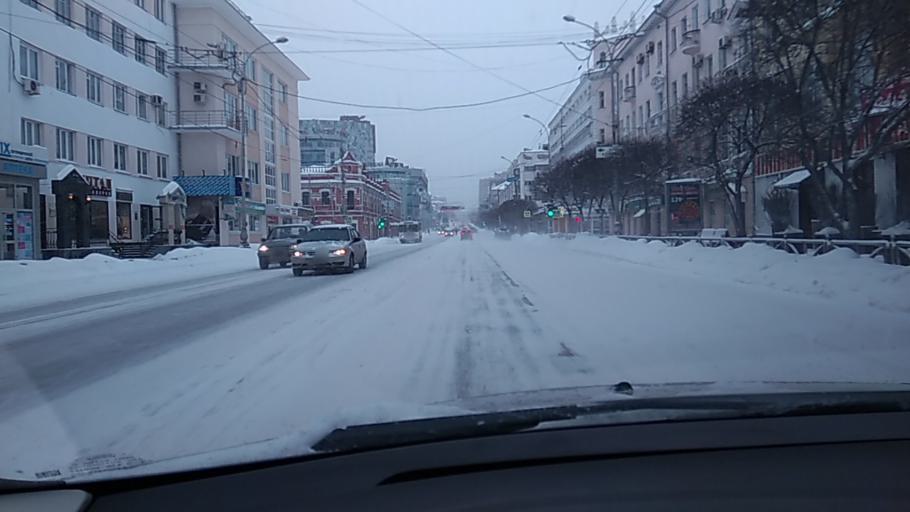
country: RU
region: Sverdlovsk
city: Yekaterinburg
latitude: 56.8334
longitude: 60.5937
